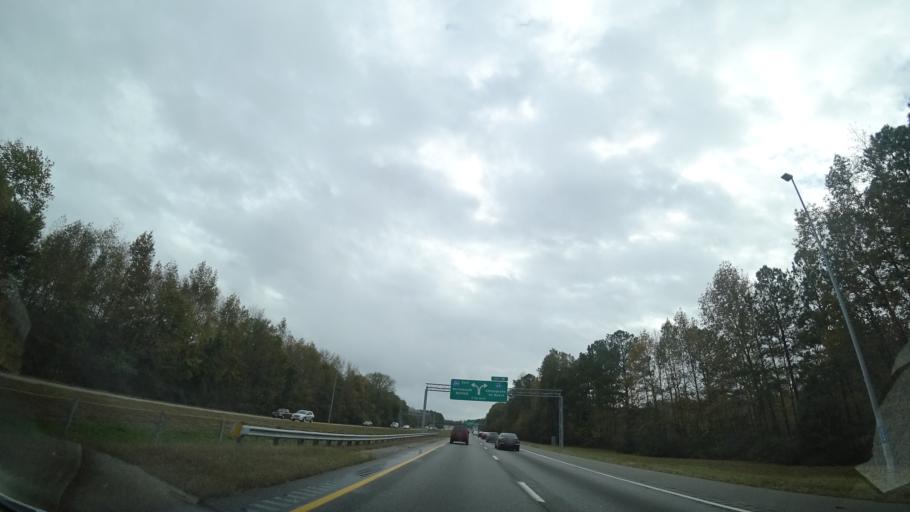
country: US
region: Virginia
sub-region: City of Portsmouth
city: Portsmouth Heights
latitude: 36.7955
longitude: -76.4277
